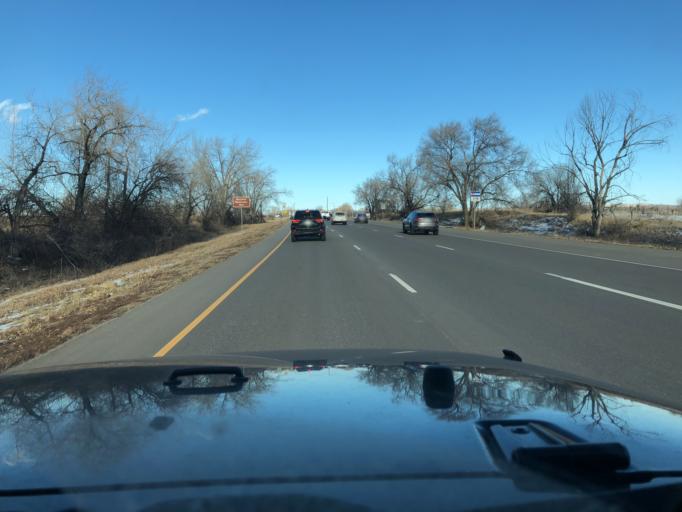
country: US
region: Colorado
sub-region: Boulder County
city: Boulder
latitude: 40.0480
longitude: -105.2369
